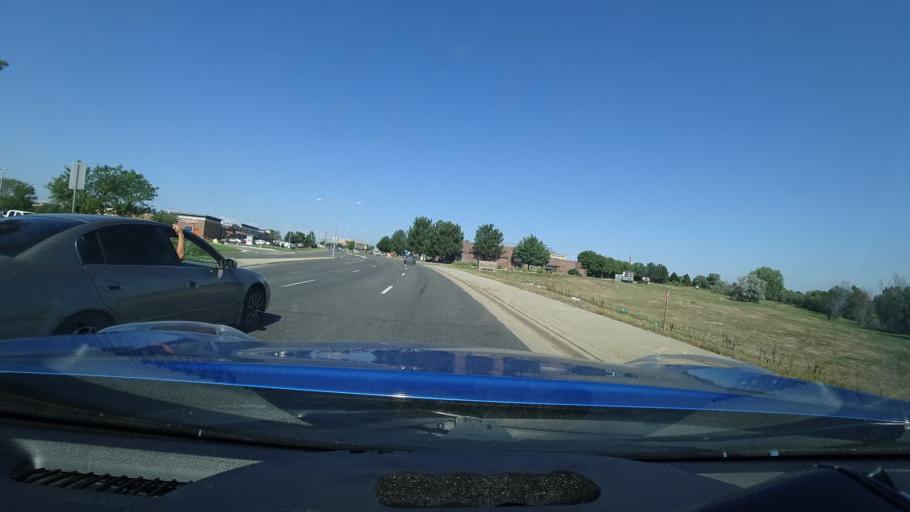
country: US
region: Colorado
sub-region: Adams County
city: Aurora
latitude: 39.7087
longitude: -104.8068
